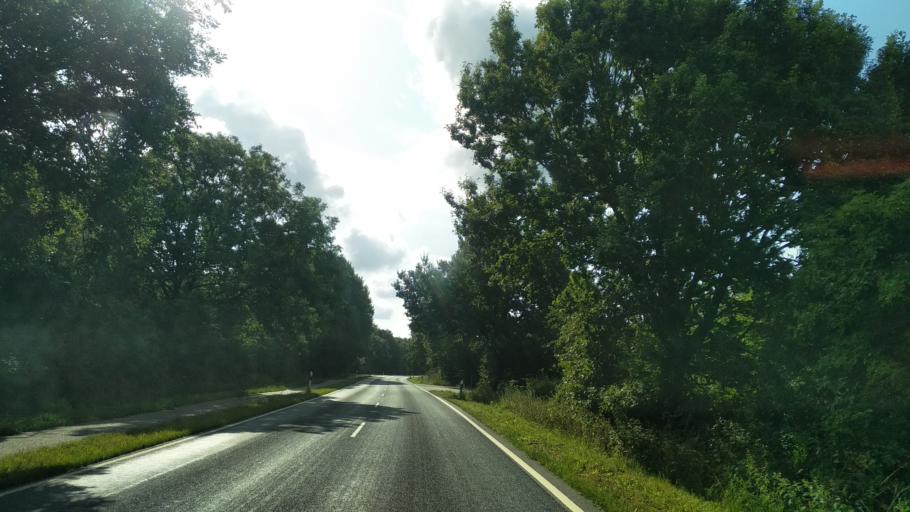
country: DE
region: Schleswig-Holstein
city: Busdorf
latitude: 54.4868
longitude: 9.5595
